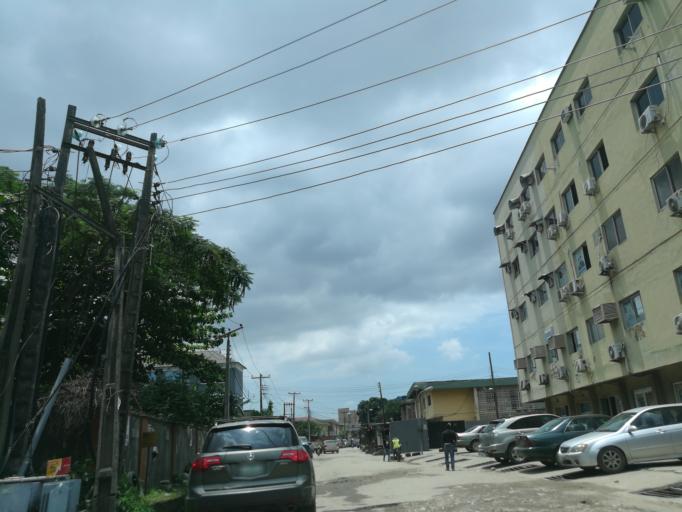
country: NG
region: Lagos
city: Ikeja
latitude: 6.6003
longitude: 3.3496
